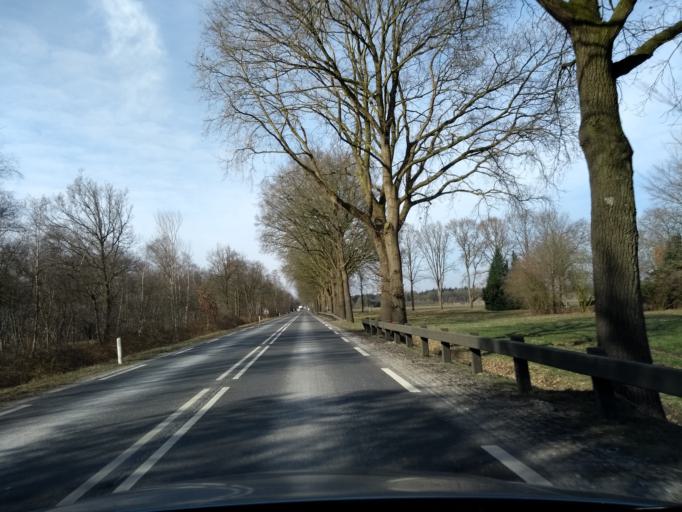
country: NL
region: Overijssel
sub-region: Gemeente Twenterand
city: Westerhaar-Vriezenveensewijk
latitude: 52.4901
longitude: 6.6830
